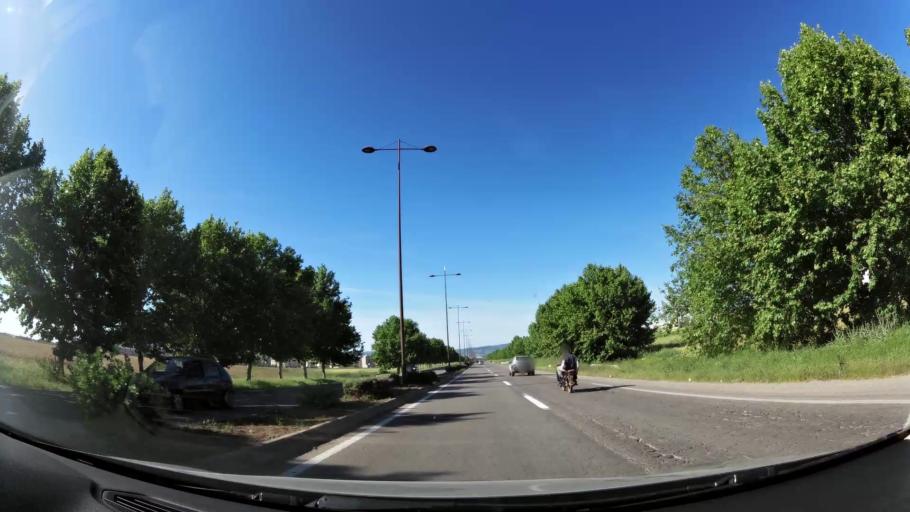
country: MA
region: Fes-Boulemane
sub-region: Fes
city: Fes
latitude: 34.0032
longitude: -5.0231
